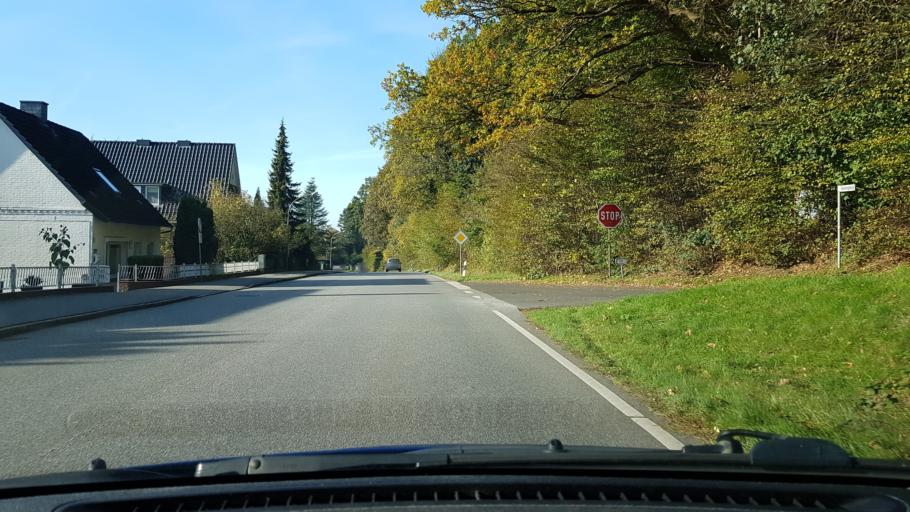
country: DE
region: Schleswig-Holstein
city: Escheburg
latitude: 53.4619
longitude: 10.3199
